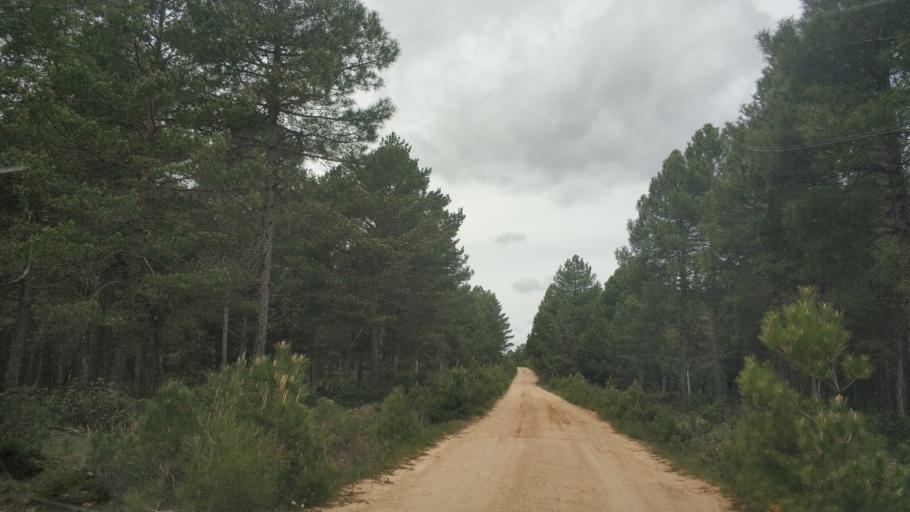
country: ES
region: Castille and Leon
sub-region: Provincia de Soria
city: Casarejos
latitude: 41.7728
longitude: -3.0378
